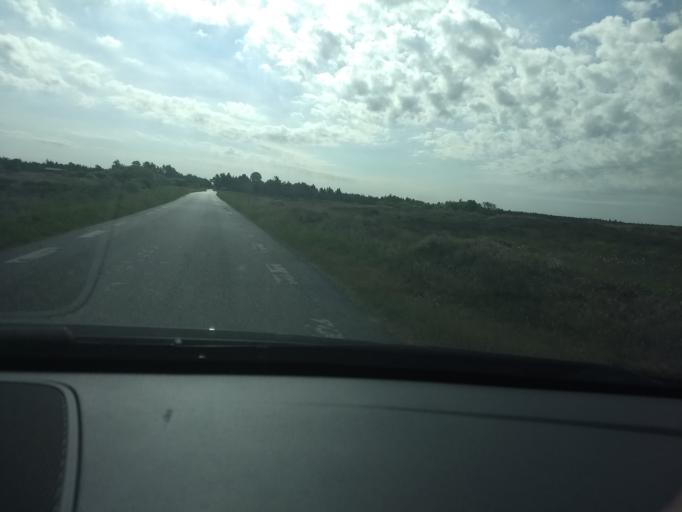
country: DE
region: Schleswig-Holstein
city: List
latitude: 55.1306
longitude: 8.5176
